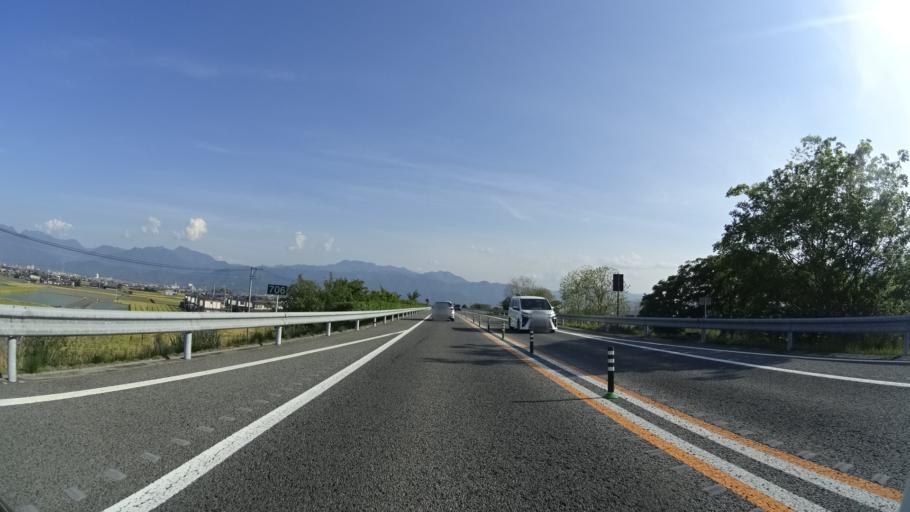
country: JP
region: Ehime
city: Saijo
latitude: 33.9447
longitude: 133.0690
